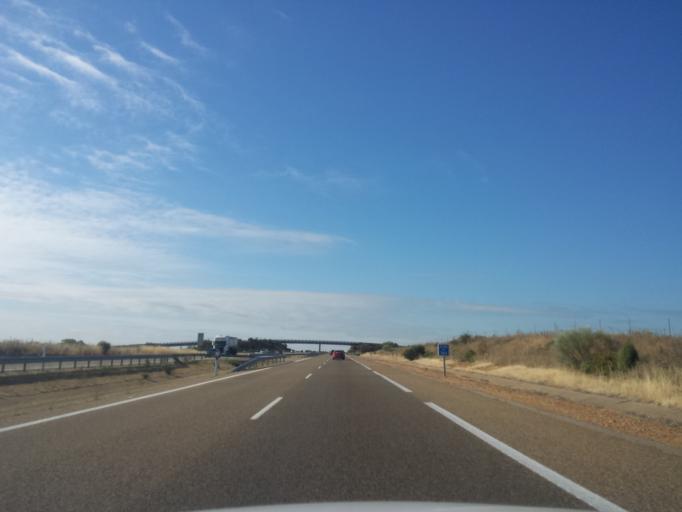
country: ES
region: Castille and Leon
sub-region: Provincia de Leon
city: Valdevimbre
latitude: 42.3874
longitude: -5.5959
